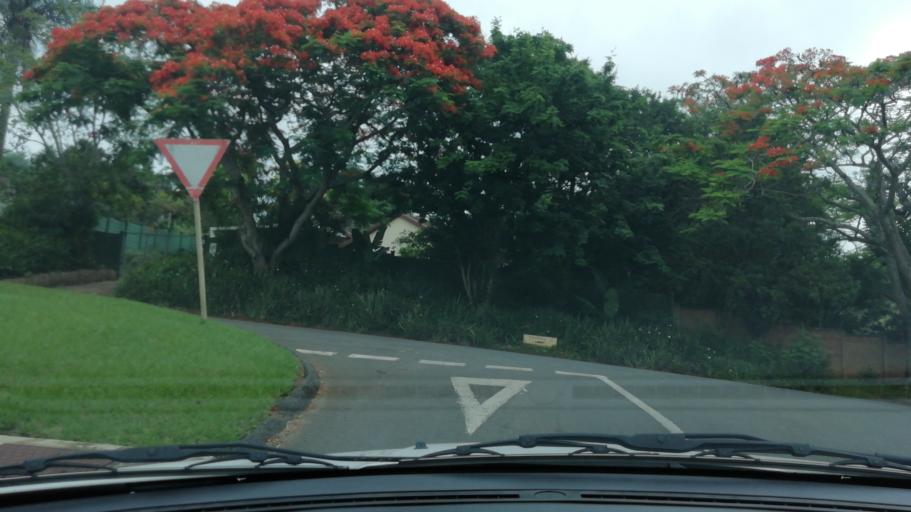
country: ZA
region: KwaZulu-Natal
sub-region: uThungulu District Municipality
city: Empangeni
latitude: -28.7584
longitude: 31.8903
